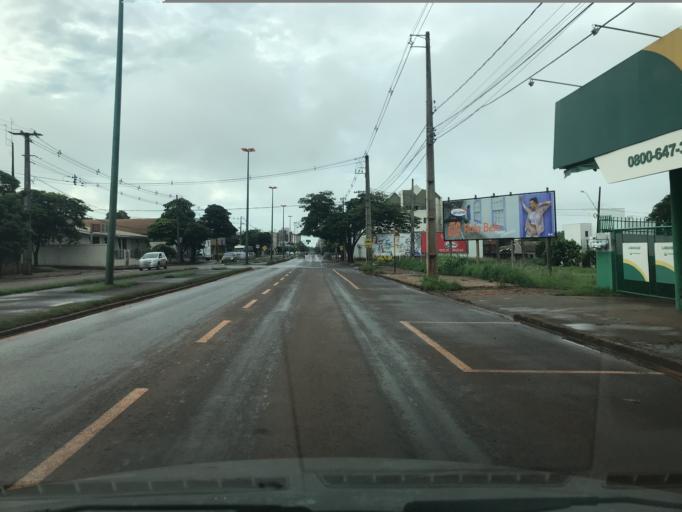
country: BR
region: Parana
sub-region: Palotina
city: Palotina
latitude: -24.2921
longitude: -53.8371
